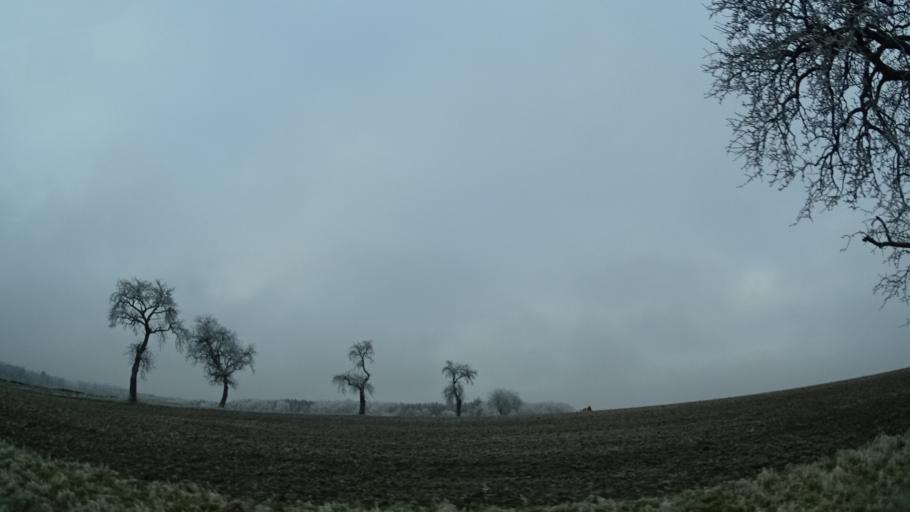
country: DE
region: Baden-Wuerttemberg
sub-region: Karlsruhe Region
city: Rosenberg
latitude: 49.4647
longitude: 9.4440
